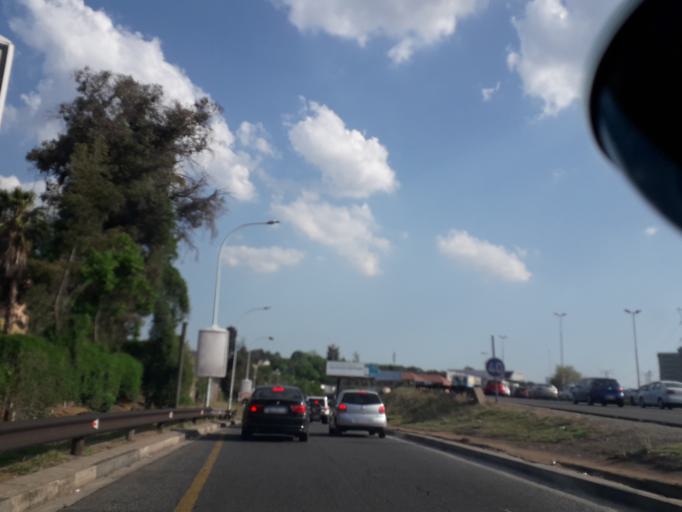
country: ZA
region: Gauteng
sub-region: City of Johannesburg Metropolitan Municipality
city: Johannesburg
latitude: -26.1270
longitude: 28.0722
